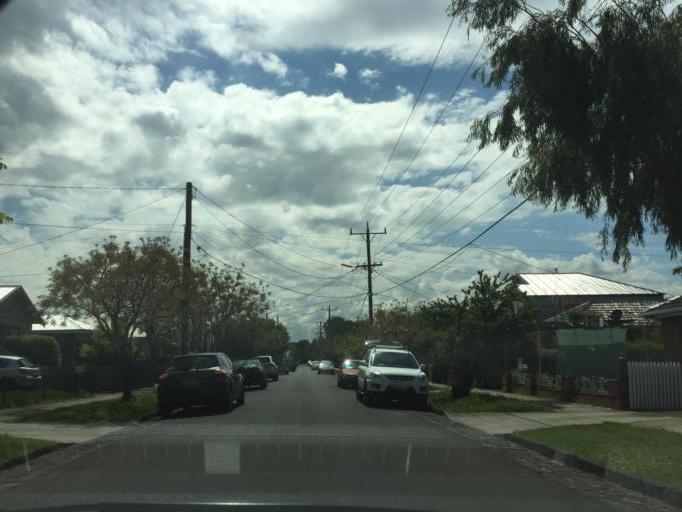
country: AU
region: Victoria
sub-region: Maribyrnong
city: West Footscray
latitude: -37.7933
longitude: 144.8798
